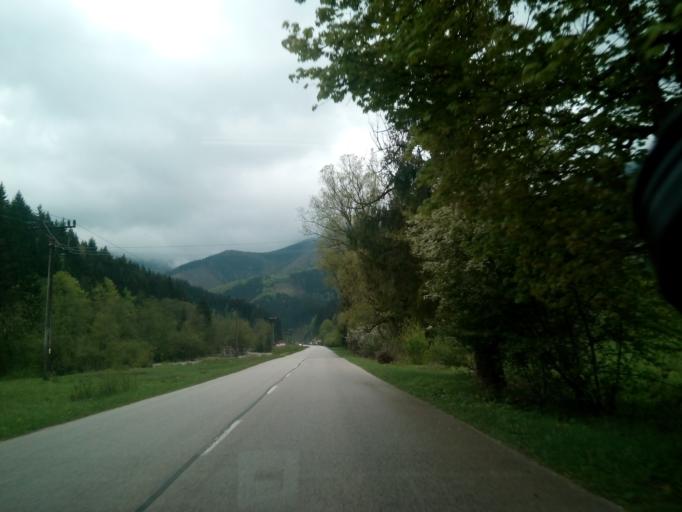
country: SK
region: Zilinsky
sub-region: Okres Zilina
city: Terchova
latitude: 49.2338
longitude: 19.0391
